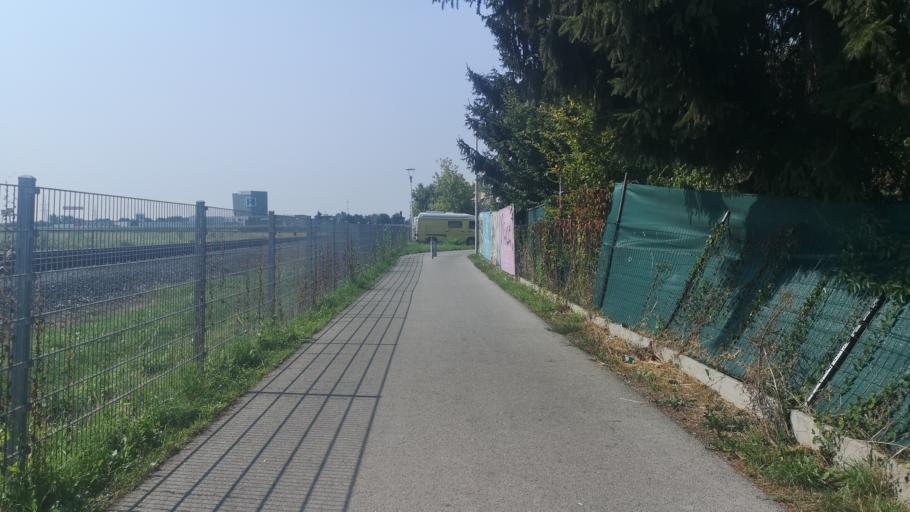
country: AT
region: Styria
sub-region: Politischer Bezirk Graz-Umgebung
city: Seiersberg
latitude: 47.0168
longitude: 15.4044
